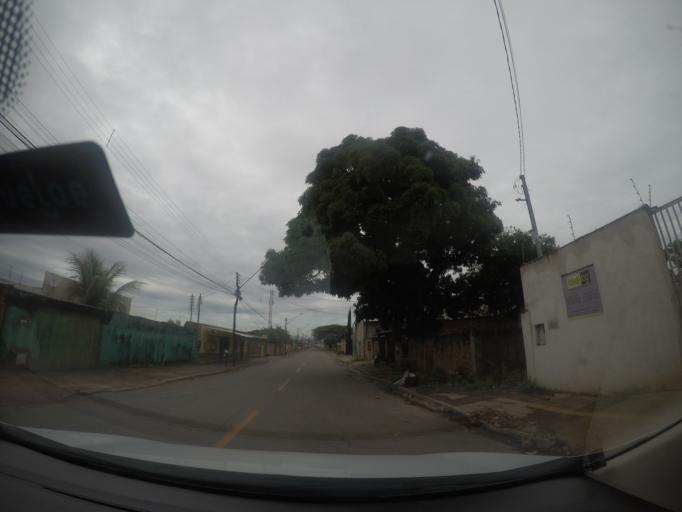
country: BR
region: Goias
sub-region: Goiania
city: Goiania
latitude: -16.6542
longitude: -49.3162
